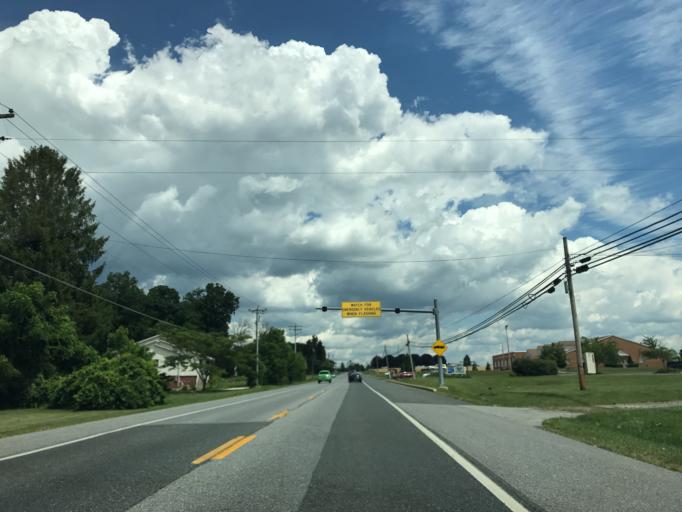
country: US
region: Maryland
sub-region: Harford County
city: Jarrettsville
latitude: 39.6127
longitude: -76.4775
